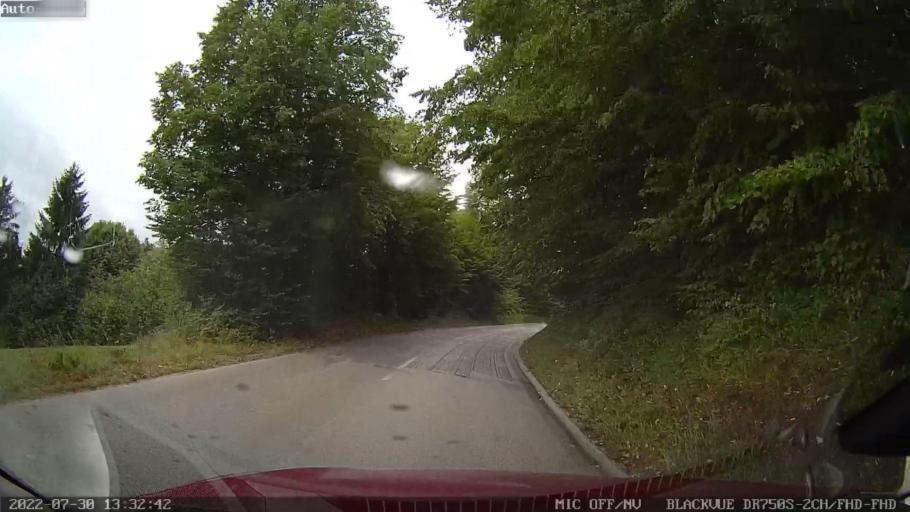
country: SI
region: Zuzemberk
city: Zuzemberk
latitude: 45.8457
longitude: 14.9361
